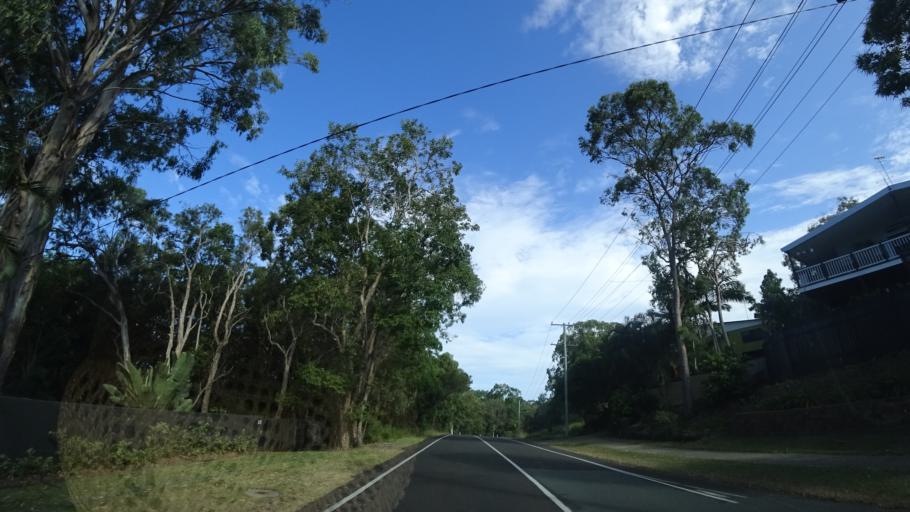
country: AU
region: Queensland
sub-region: Sunshine Coast
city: Coolum Beach
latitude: -26.5589
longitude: 153.0895
